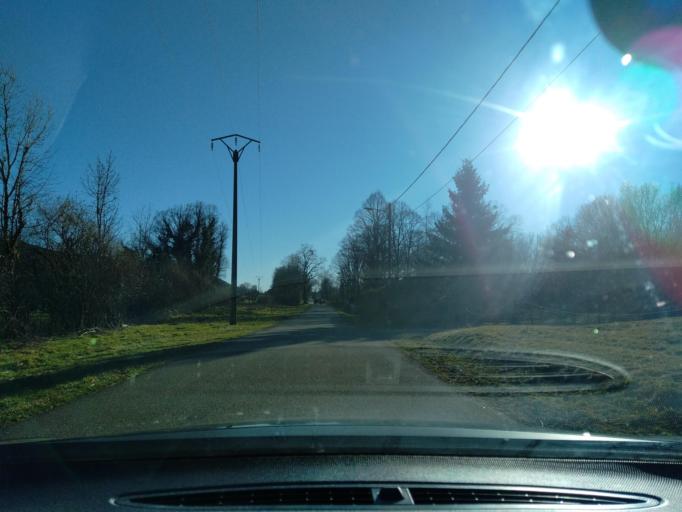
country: FR
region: Franche-Comte
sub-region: Departement du Jura
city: Poligny
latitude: 46.7244
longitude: 5.7454
